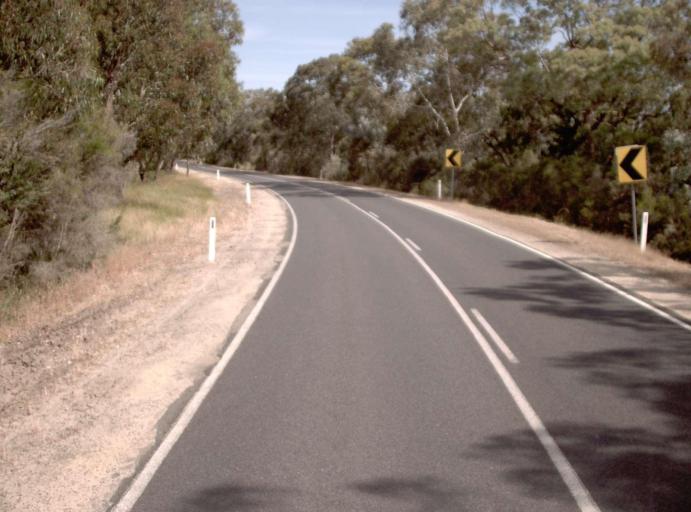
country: AU
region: Victoria
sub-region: Wellington
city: Sale
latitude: -38.2498
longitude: 147.1327
